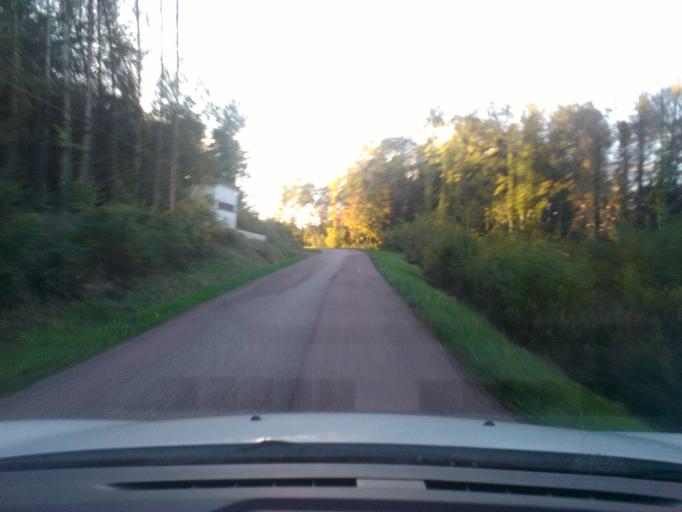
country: FR
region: Lorraine
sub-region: Departement des Vosges
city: Vincey
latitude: 48.3314
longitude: 6.3173
